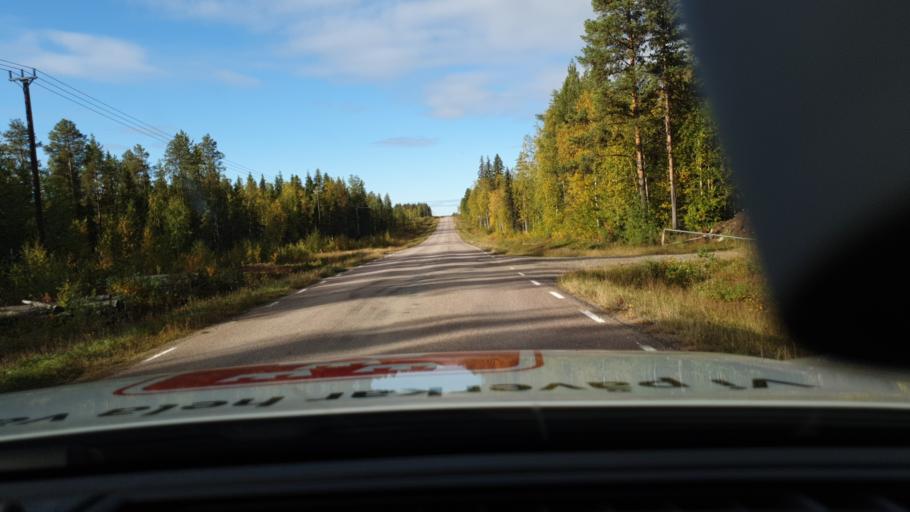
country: SE
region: Norrbotten
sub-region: Pajala Kommun
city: Pajala
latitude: 67.1933
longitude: 23.3223
